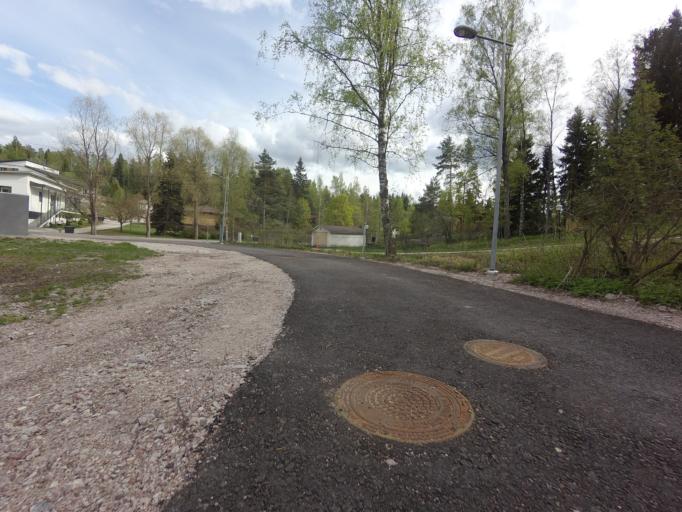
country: FI
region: Uusimaa
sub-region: Helsinki
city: Kauniainen
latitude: 60.1854
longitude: 24.7175
